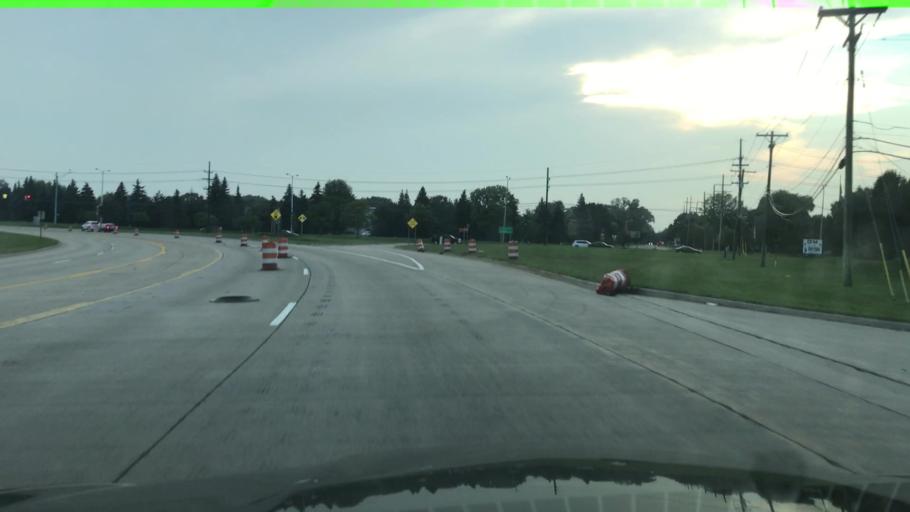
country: US
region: Michigan
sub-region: Macomb County
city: Sterling Heights
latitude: 42.6016
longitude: -83.0490
